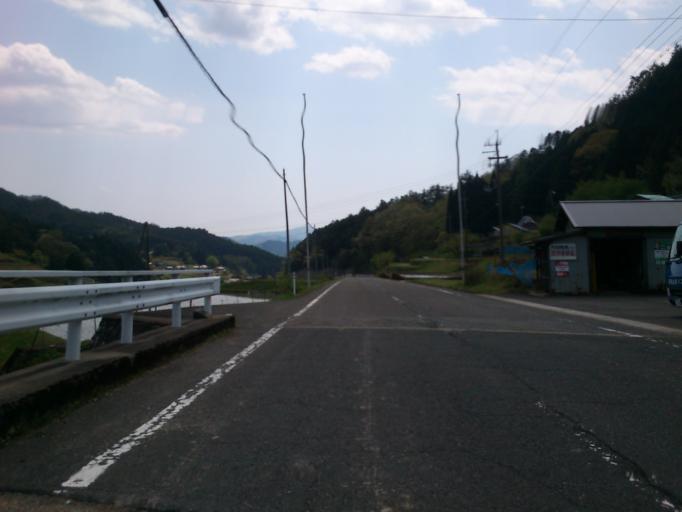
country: JP
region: Kyoto
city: Fukuchiyama
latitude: 35.3884
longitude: 134.9791
